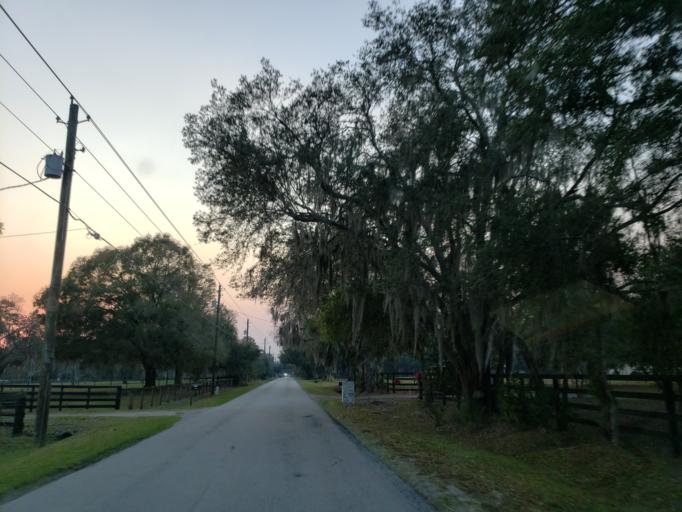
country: US
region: Florida
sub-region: Hillsborough County
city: Fish Hawk
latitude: 27.8428
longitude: -82.1954
